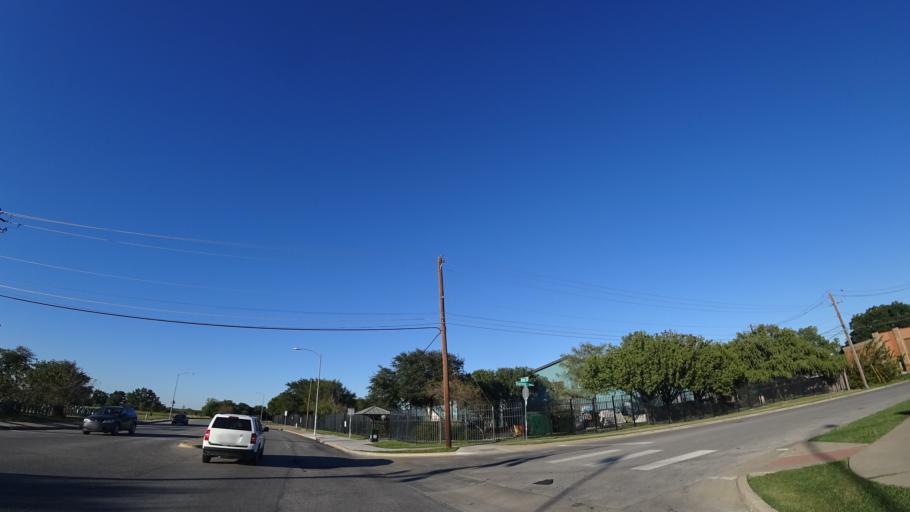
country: US
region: Texas
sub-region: Travis County
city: Austin
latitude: 30.2300
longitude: -97.7063
